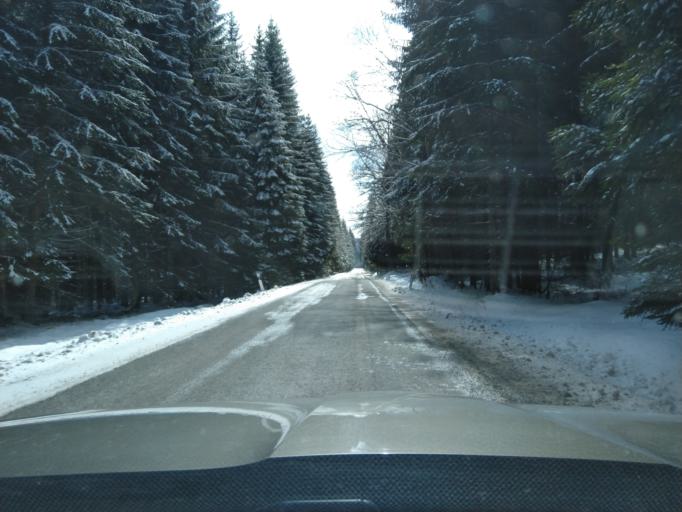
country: CZ
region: Jihocesky
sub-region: Okres Prachatice
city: Stachy
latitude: 49.0534
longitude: 13.6593
